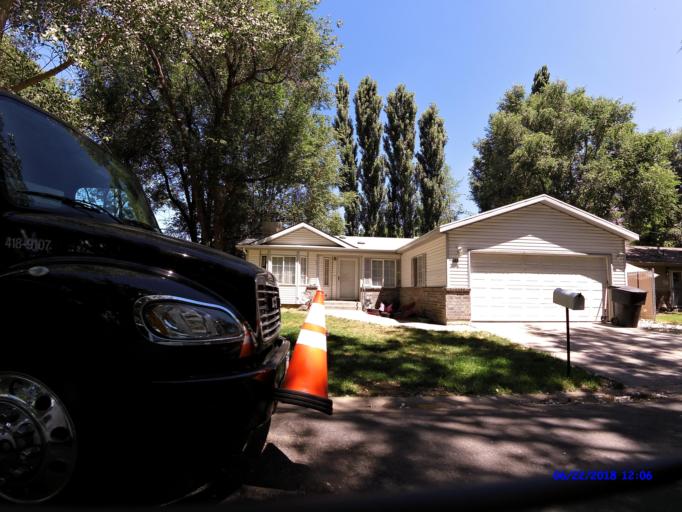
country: US
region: Utah
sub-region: Weber County
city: Ogden
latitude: 41.2373
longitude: -111.9545
